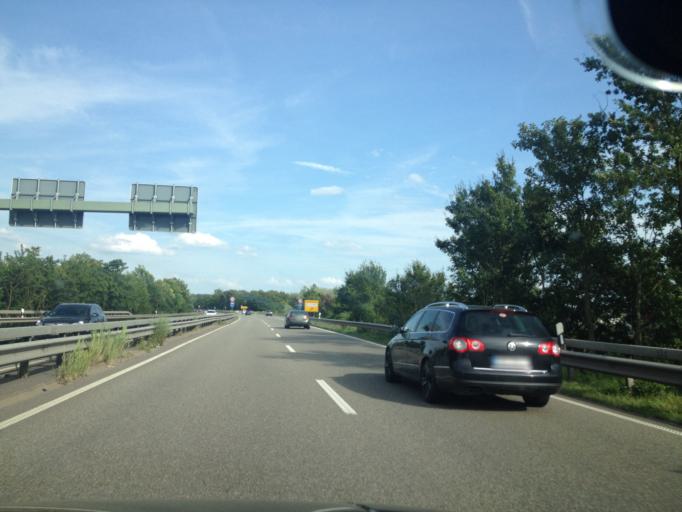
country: DE
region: Rheinland-Pfalz
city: Germersheim
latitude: 49.2315
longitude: 8.3657
